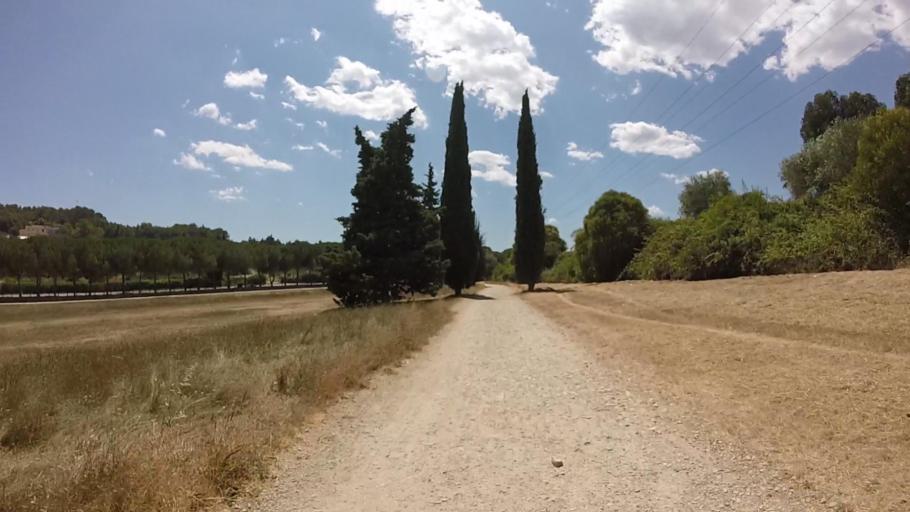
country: FR
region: Provence-Alpes-Cote d'Azur
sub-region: Departement des Alpes-Maritimes
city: Mougins
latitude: 43.5953
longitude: 7.0078
